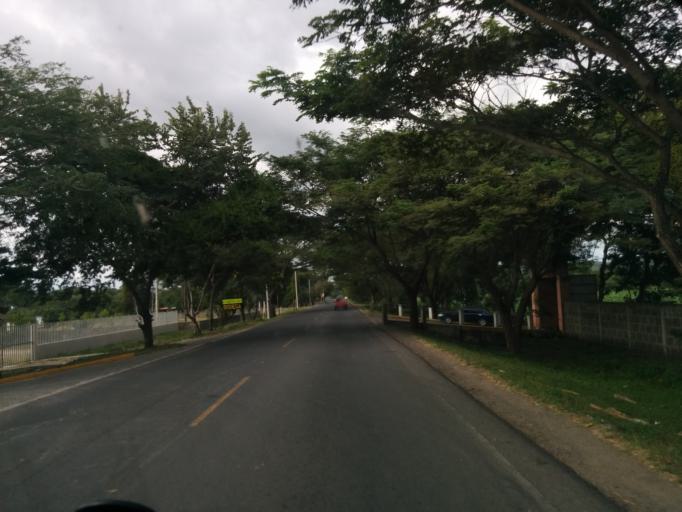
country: NI
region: Esteli
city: Esteli
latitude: 13.1284
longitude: -86.3644
